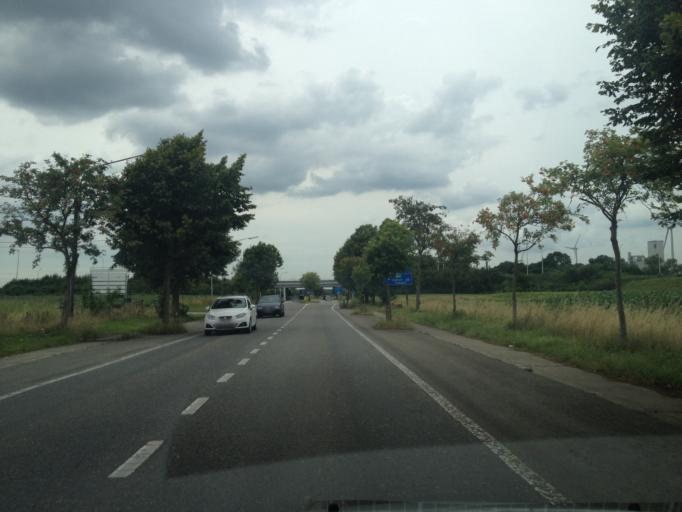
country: BE
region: Flanders
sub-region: Provincie West-Vlaanderen
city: Ieper
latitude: 50.8677
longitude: 2.8747
